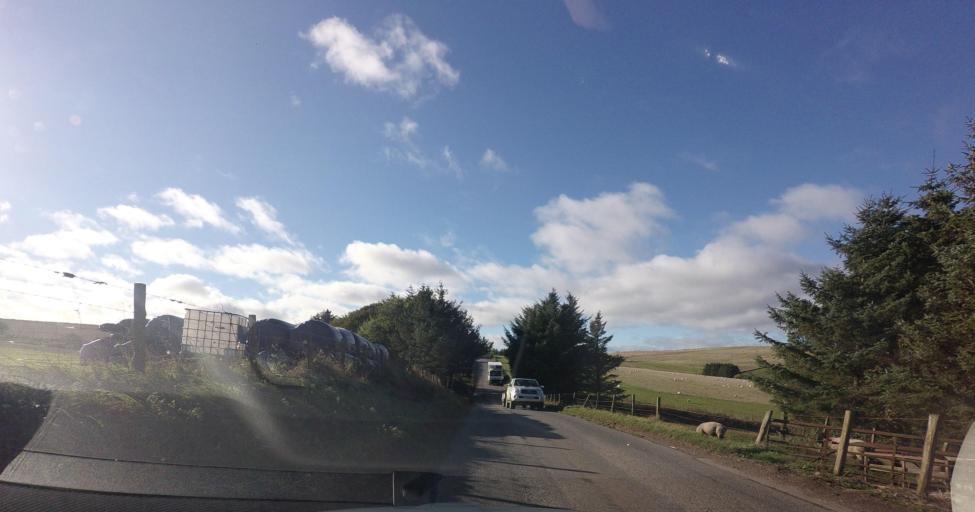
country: GB
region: Scotland
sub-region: Aberdeenshire
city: Macduff
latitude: 57.6642
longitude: -2.3159
